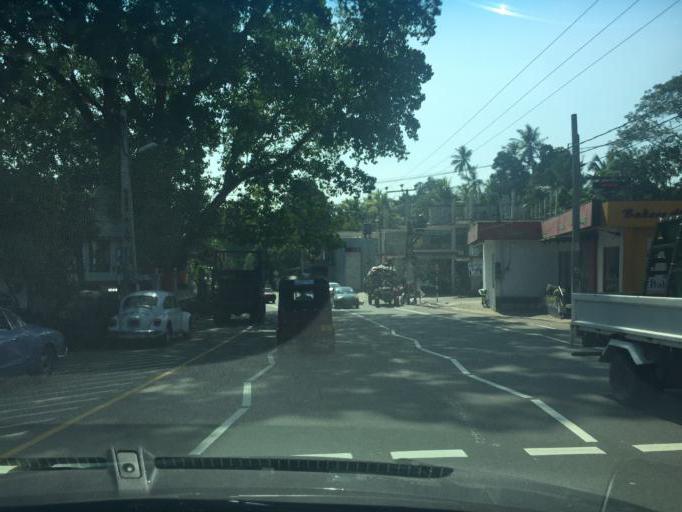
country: LK
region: Western
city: Moratuwa
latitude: 6.7974
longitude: 79.9103
